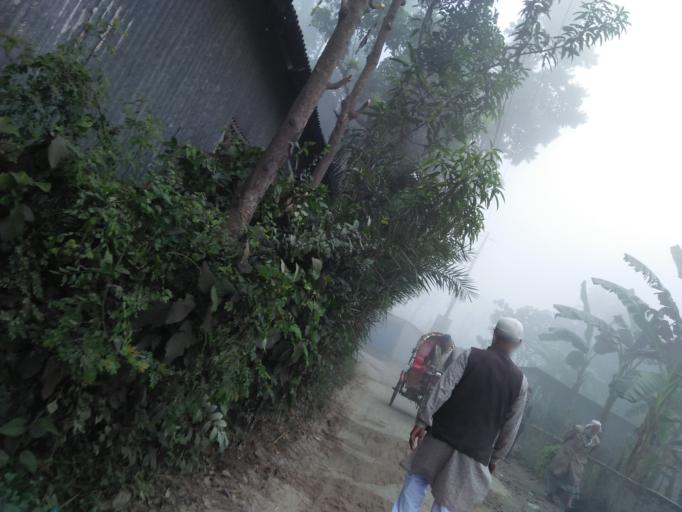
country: BD
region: Dhaka
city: Azimpur
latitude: 23.6898
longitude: 90.3045
